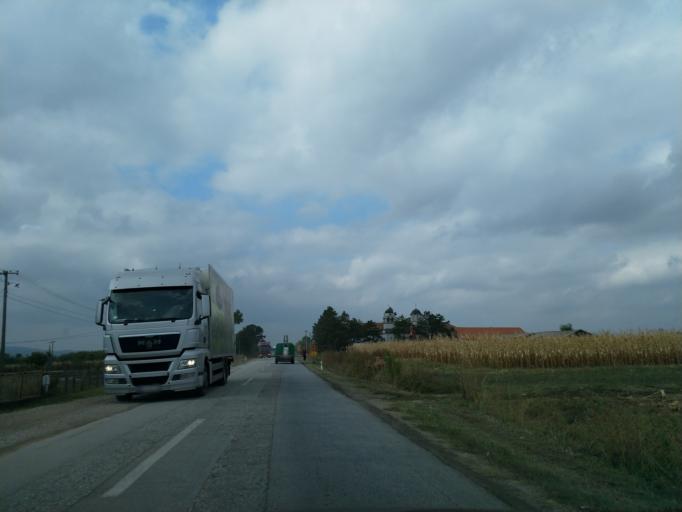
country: RS
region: Central Serbia
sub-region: Sumadijski Okrug
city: Kragujevac
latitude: 44.0982
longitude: 20.8602
